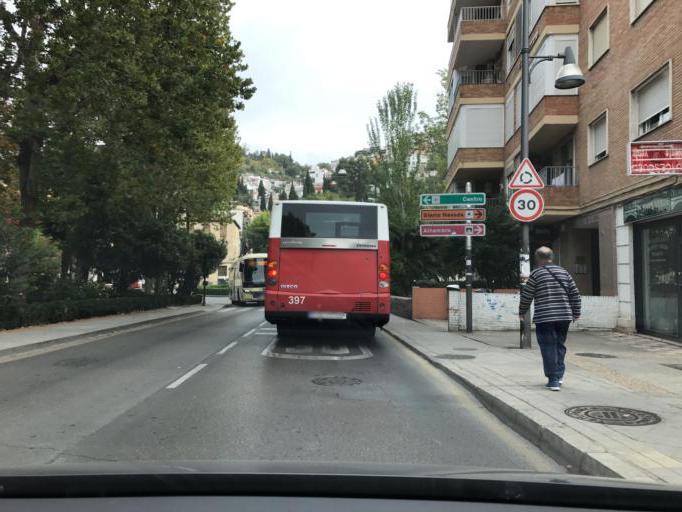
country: ES
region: Andalusia
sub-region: Provincia de Granada
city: Granada
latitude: 37.1673
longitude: -3.5894
